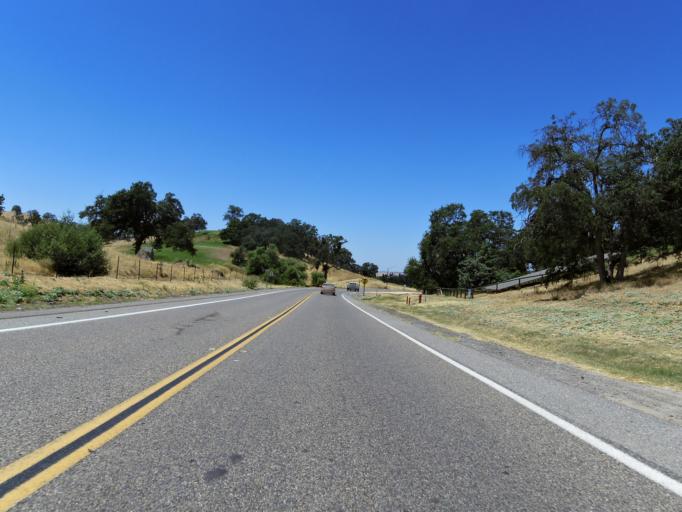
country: US
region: California
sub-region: Fresno County
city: Clovis
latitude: 36.9823
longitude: -119.6367
